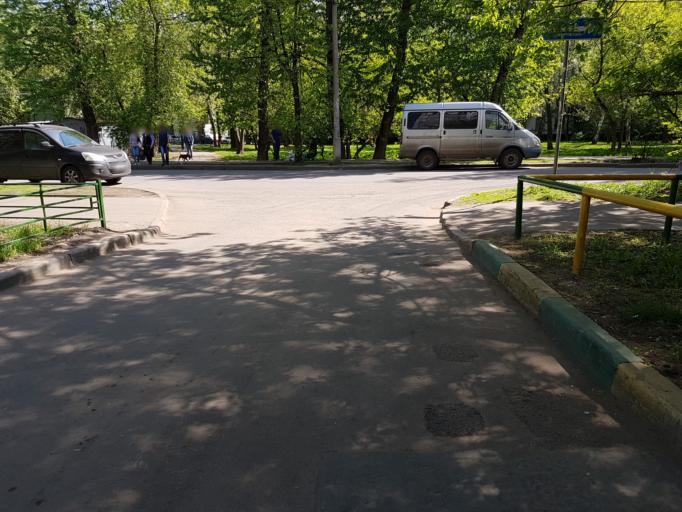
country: RU
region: Moskovskaya
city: Novogireyevo
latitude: 55.7527
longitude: 37.8218
